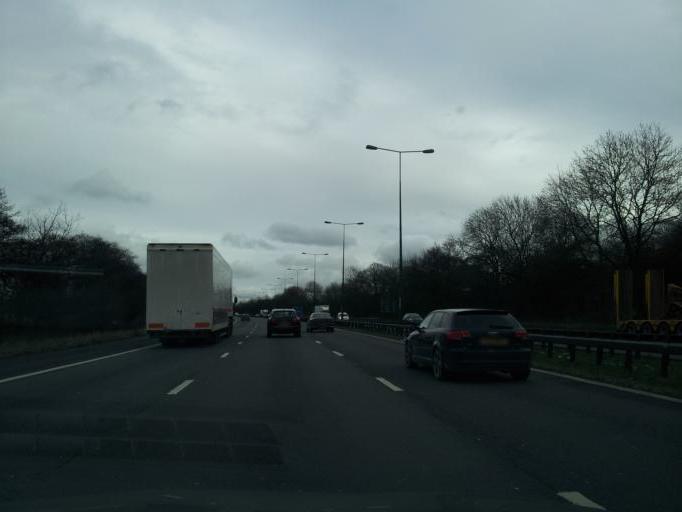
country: GB
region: England
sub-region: Staffordshire
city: Audley
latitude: 52.9950
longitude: -2.3087
